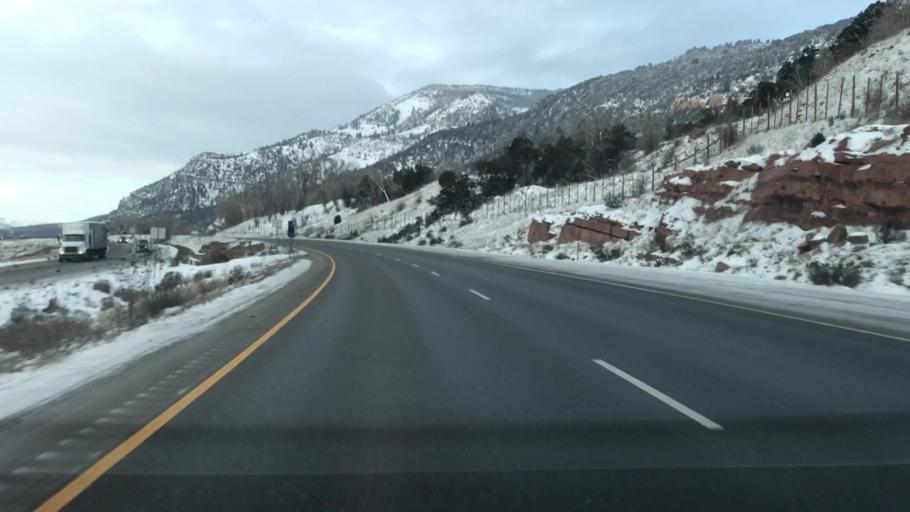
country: US
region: Colorado
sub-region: Eagle County
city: Eagle
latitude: 39.7107
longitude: -106.7136
